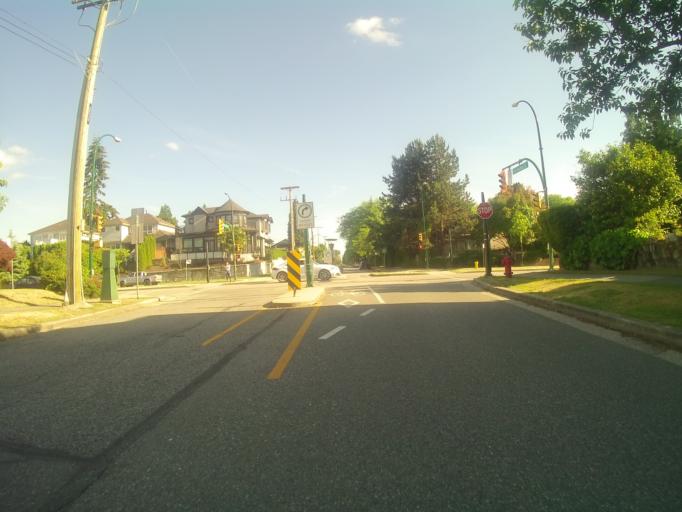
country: CA
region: British Columbia
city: Vancouver
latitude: 49.2493
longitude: -123.1204
